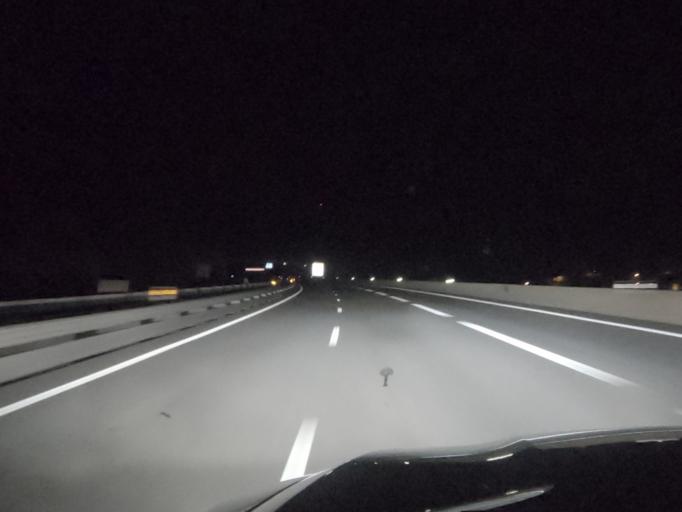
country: PT
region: Porto
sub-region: Baiao
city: Valadares
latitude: 41.2513
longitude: -7.9600
